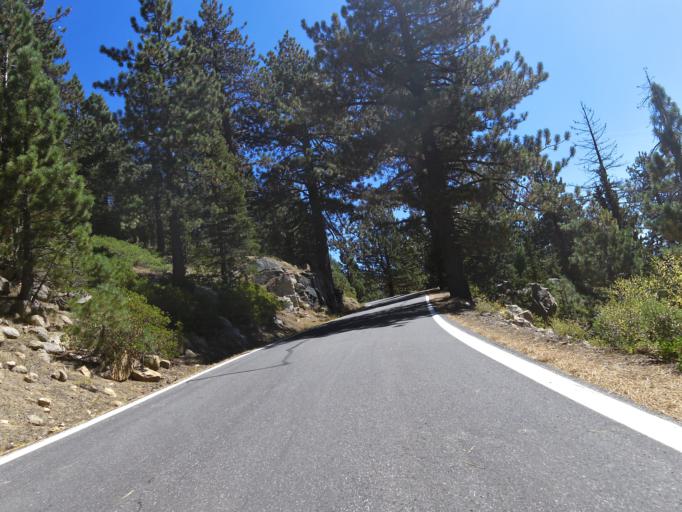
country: US
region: Nevada
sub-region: Douglas County
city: Gardnerville Ranchos
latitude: 38.5490
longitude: -119.8443
